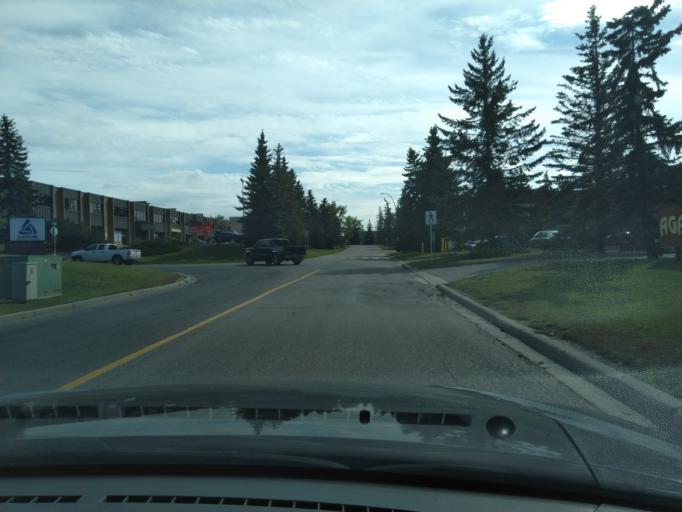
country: CA
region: Alberta
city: Calgary
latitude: 51.0773
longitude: -114.0254
